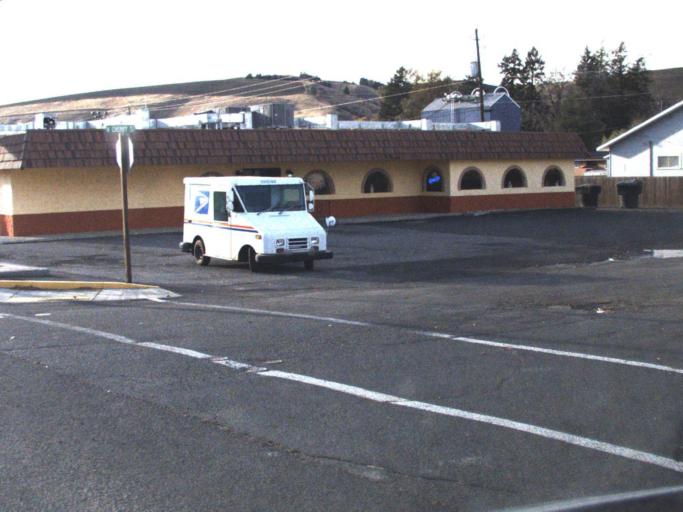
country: US
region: Washington
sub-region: Columbia County
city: Dayton
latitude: 46.3166
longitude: -117.9874
